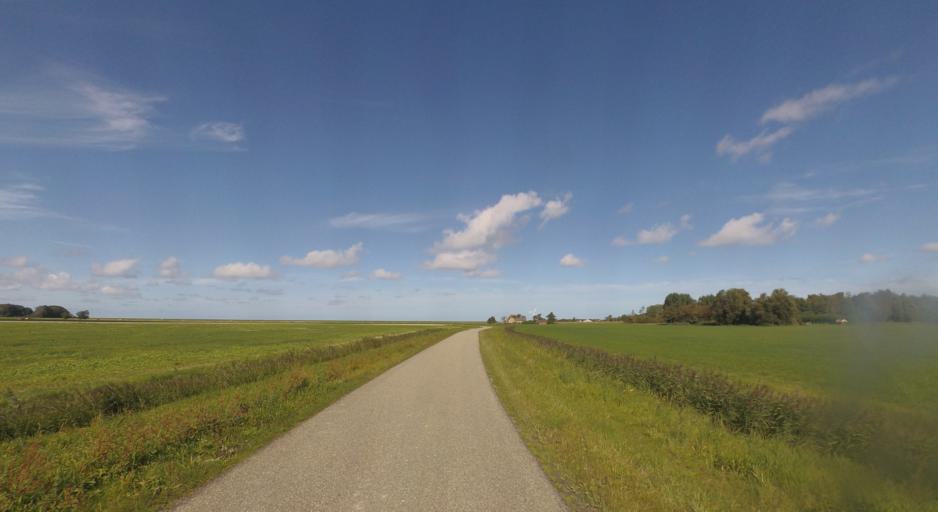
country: NL
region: Friesland
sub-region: Gemeente Dongeradeel
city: Holwerd
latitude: 53.3620
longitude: 5.8959
